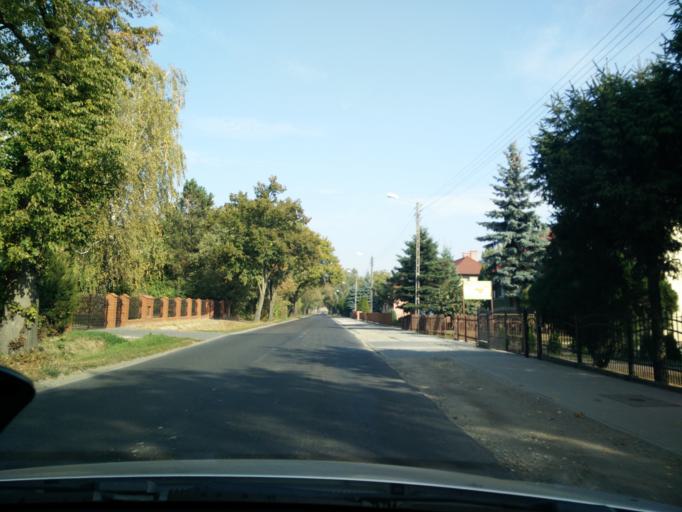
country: PL
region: Greater Poland Voivodeship
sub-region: Powiat sredzki
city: Sroda Wielkopolska
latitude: 52.2376
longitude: 17.2868
